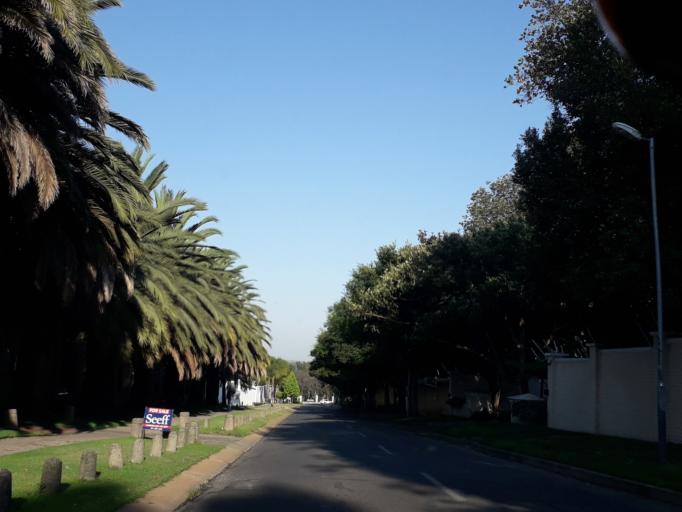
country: ZA
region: Gauteng
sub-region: City of Johannesburg Metropolitan Municipality
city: Johannesburg
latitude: -26.1156
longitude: 28.0355
